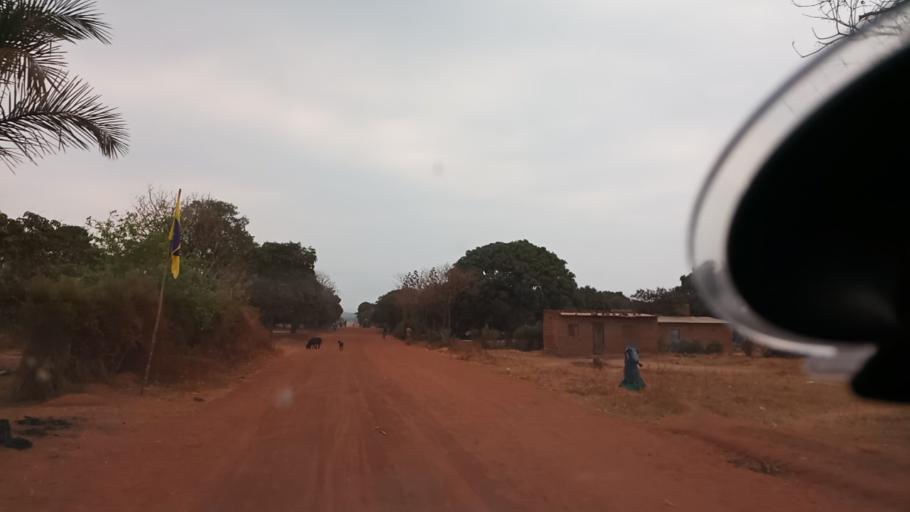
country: ZM
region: Luapula
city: Nchelenge
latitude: -9.2770
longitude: 28.3252
